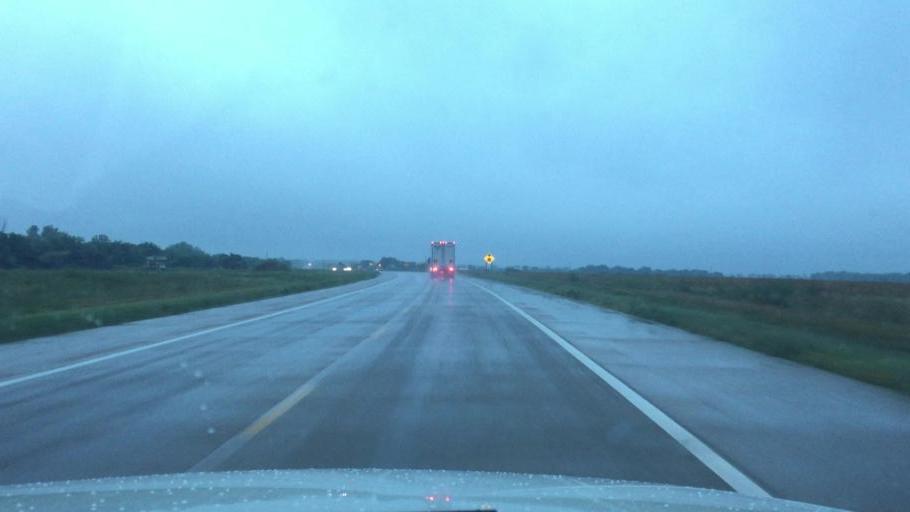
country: US
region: Kansas
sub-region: Neosho County
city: Chanute
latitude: 37.5336
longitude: -95.4713
